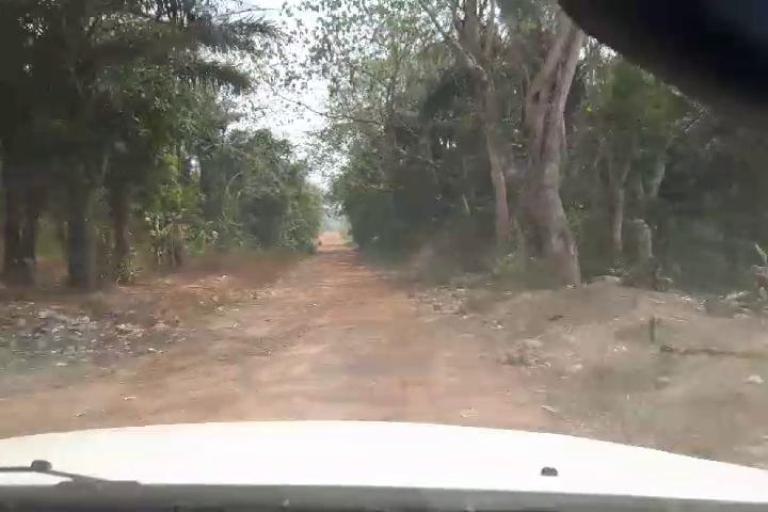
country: SL
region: Northern Province
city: Bumbuna
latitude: 8.9468
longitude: -11.8123
